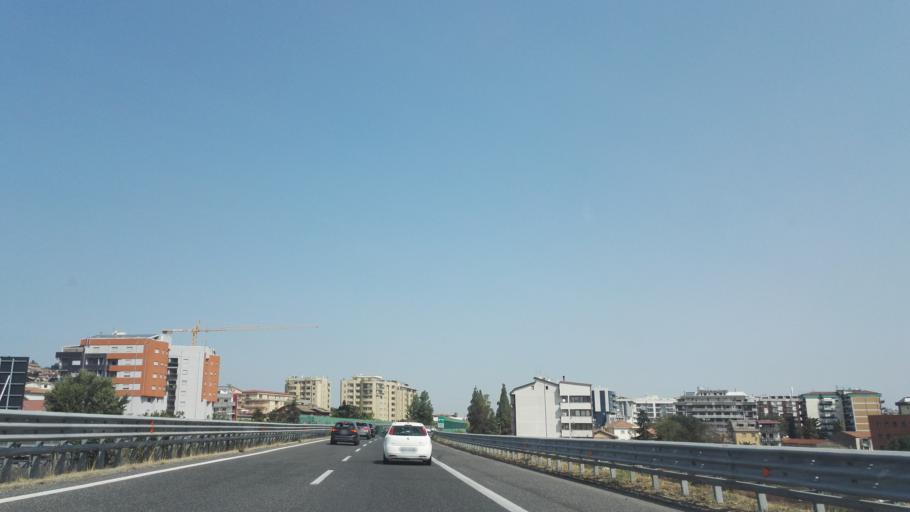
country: IT
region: Calabria
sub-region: Provincia di Cosenza
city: Cosenza
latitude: 39.3204
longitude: 16.2406
